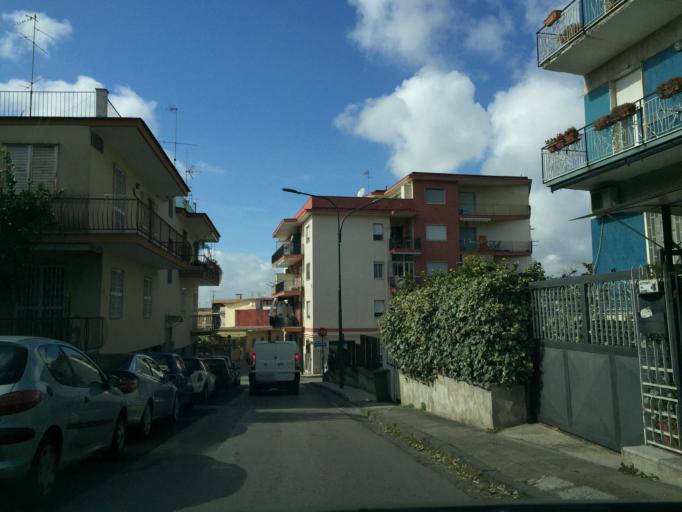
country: IT
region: Campania
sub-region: Provincia di Napoli
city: San Sebastiano al Vesuvio
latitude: 40.8483
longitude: 14.3688
